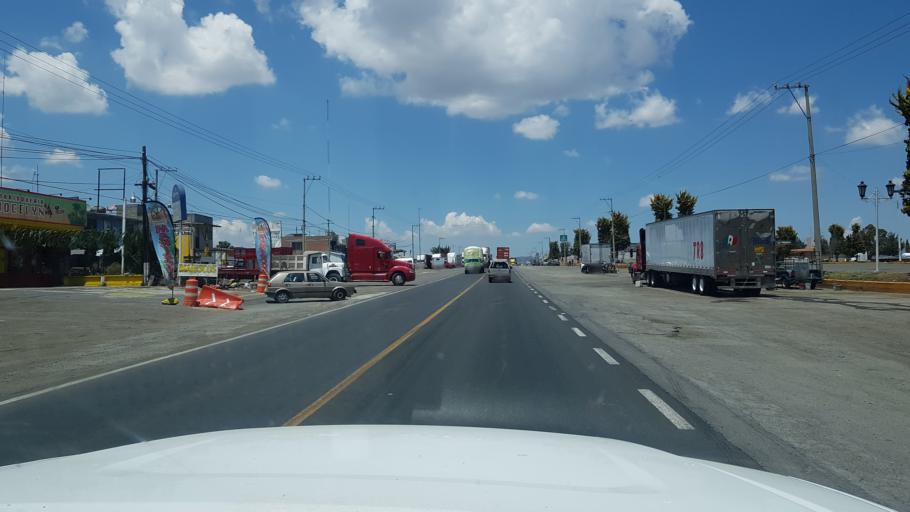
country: MX
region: Hidalgo
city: Calpulalpan
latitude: 19.5860
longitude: -98.5446
